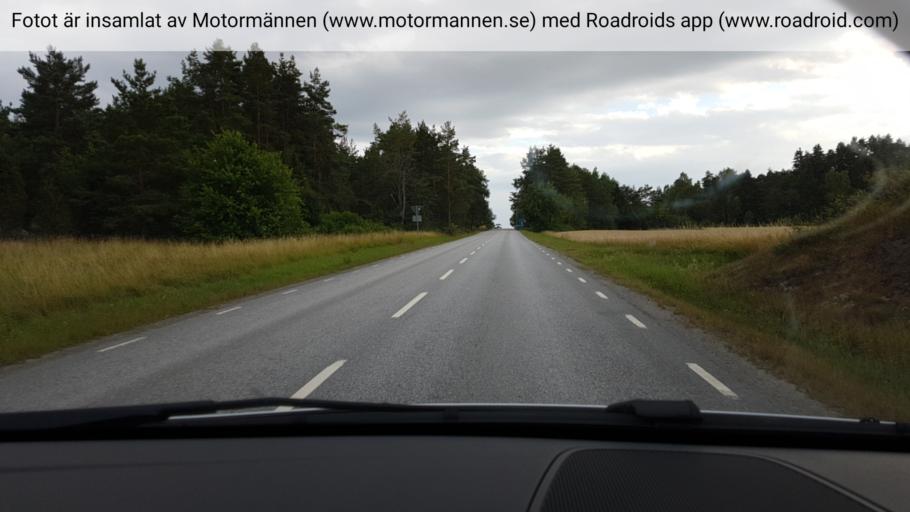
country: SE
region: Uppsala
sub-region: Uppsala Kommun
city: Alsike
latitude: 59.7163
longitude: 17.7291
